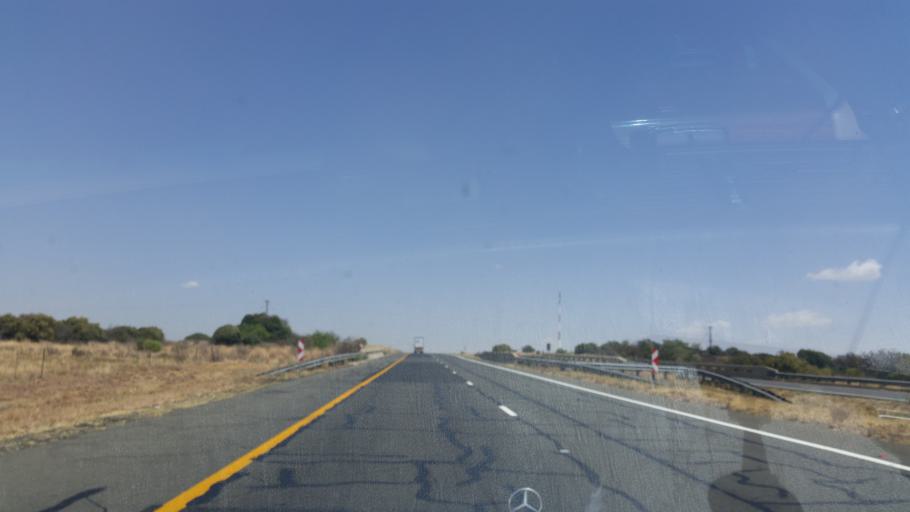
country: ZA
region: Orange Free State
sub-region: Lejweleputswa District Municipality
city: Brandfort
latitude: -28.9055
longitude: 26.4635
